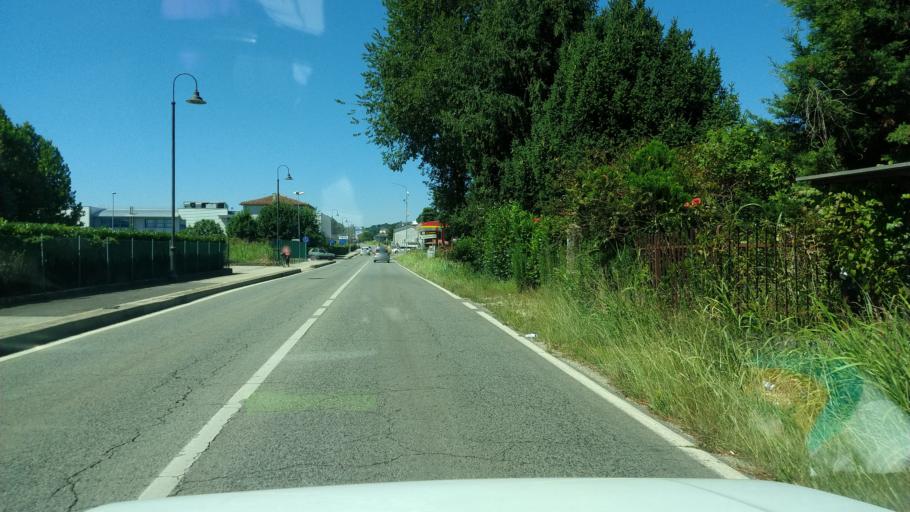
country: IT
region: Veneto
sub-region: Provincia di Vicenza
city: Mure
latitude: 45.7279
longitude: 11.6228
